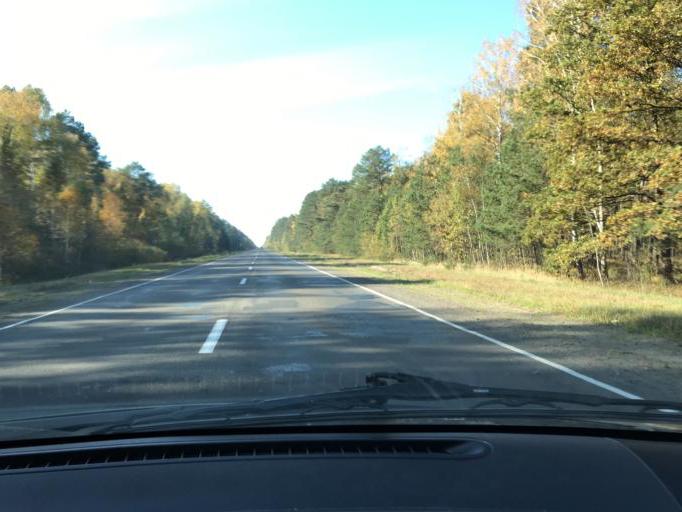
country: BY
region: Brest
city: Asnyezhytsy
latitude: 52.2485
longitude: 26.2470
